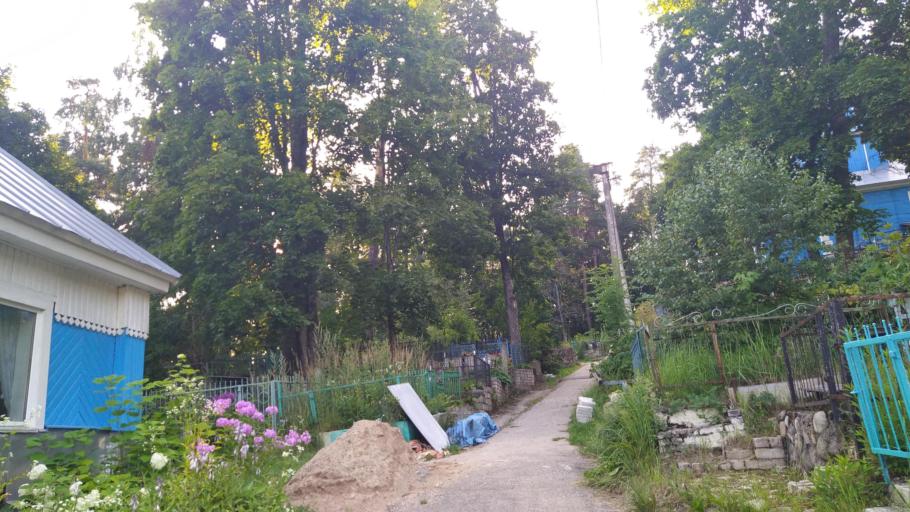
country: RU
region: Pskov
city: Pushkinskiye Gory
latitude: 57.0245
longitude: 28.9173
